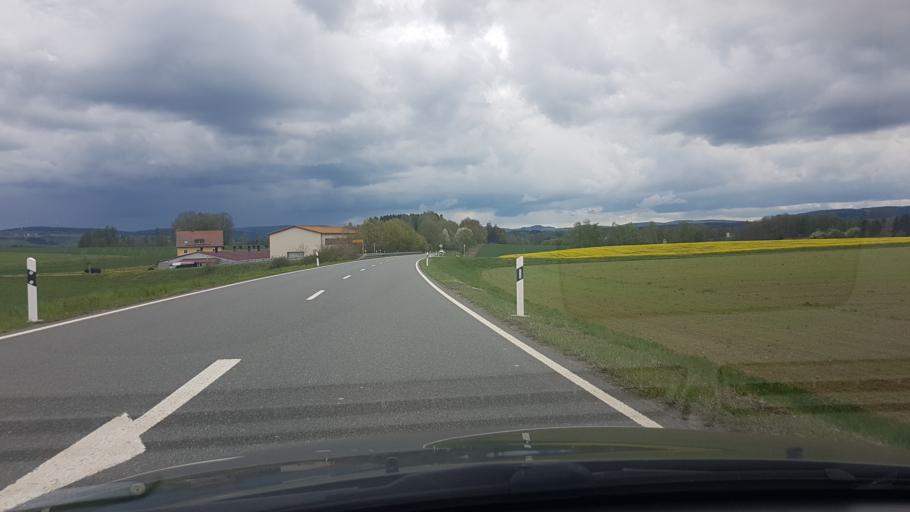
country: DE
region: Bavaria
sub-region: Upper Palatinate
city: Berg
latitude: 49.8393
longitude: 12.1415
